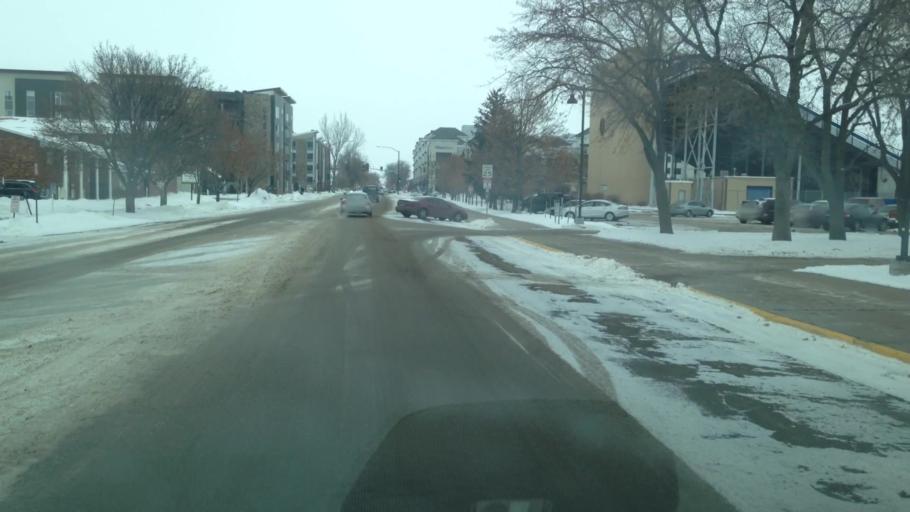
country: US
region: Idaho
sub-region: Madison County
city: Rexburg
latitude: 43.8197
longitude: -111.7867
